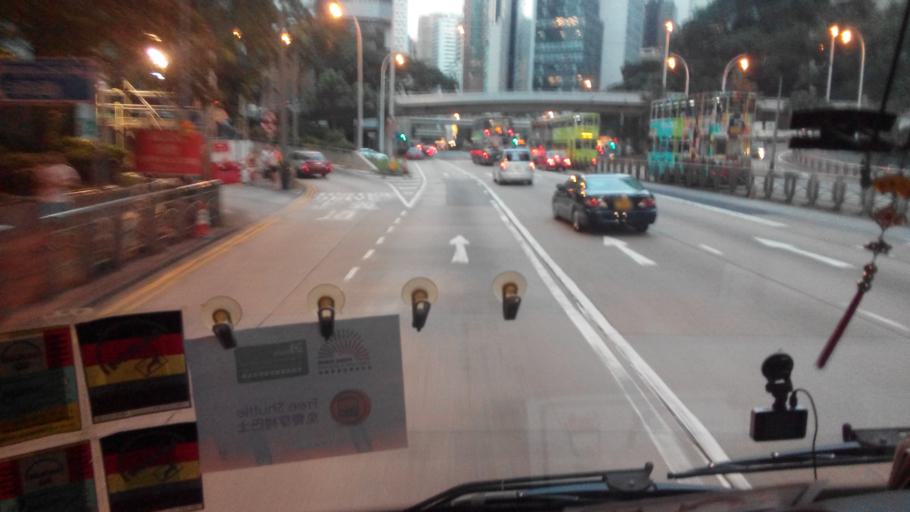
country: HK
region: Central and Western
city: Central
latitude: 22.2766
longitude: 114.1636
